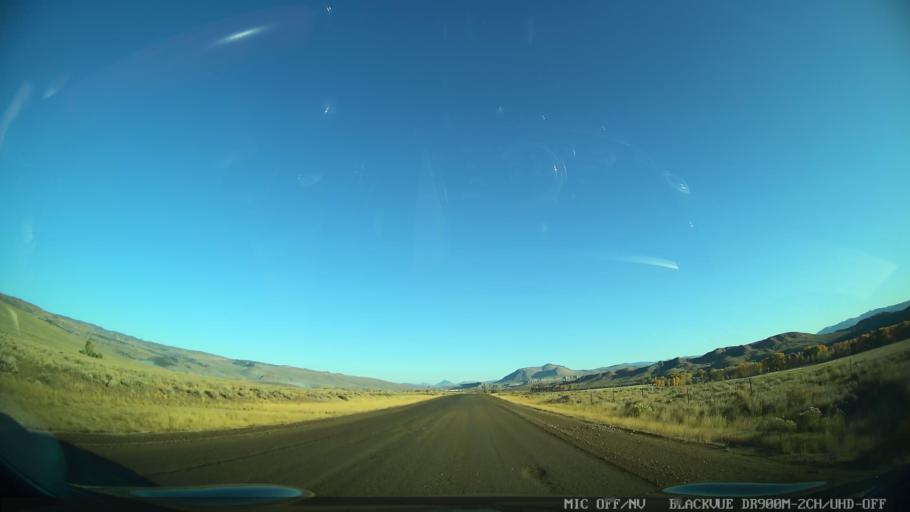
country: US
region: Colorado
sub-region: Grand County
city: Kremmling
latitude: 40.0233
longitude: -106.3892
